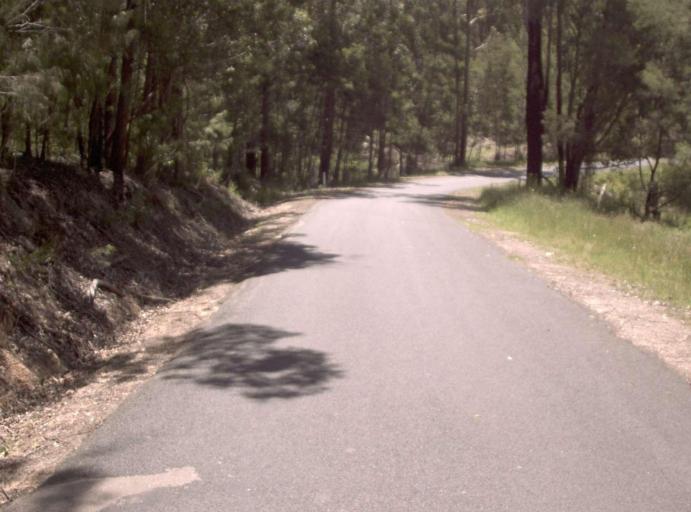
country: AU
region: New South Wales
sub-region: Bombala
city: Bombala
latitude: -37.5189
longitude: 148.9290
